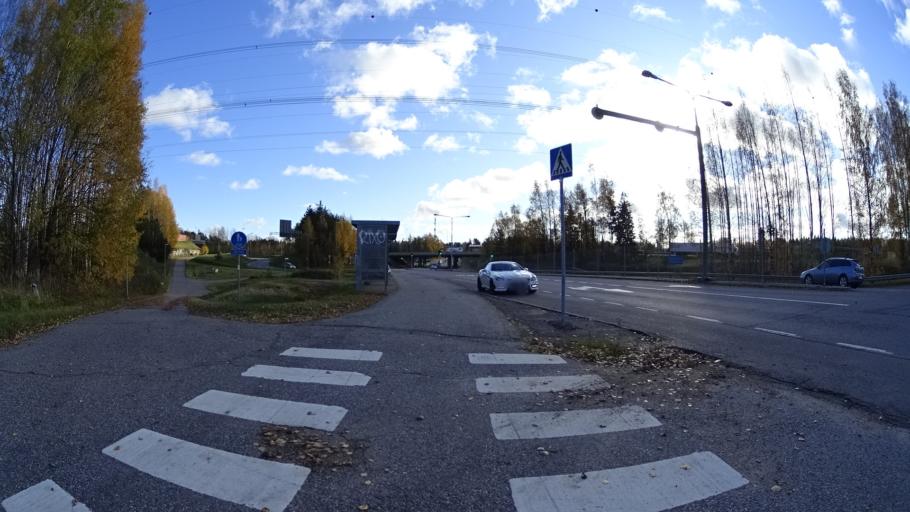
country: FI
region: Uusimaa
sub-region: Helsinki
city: Teekkarikylae
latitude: 60.2956
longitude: 24.8592
